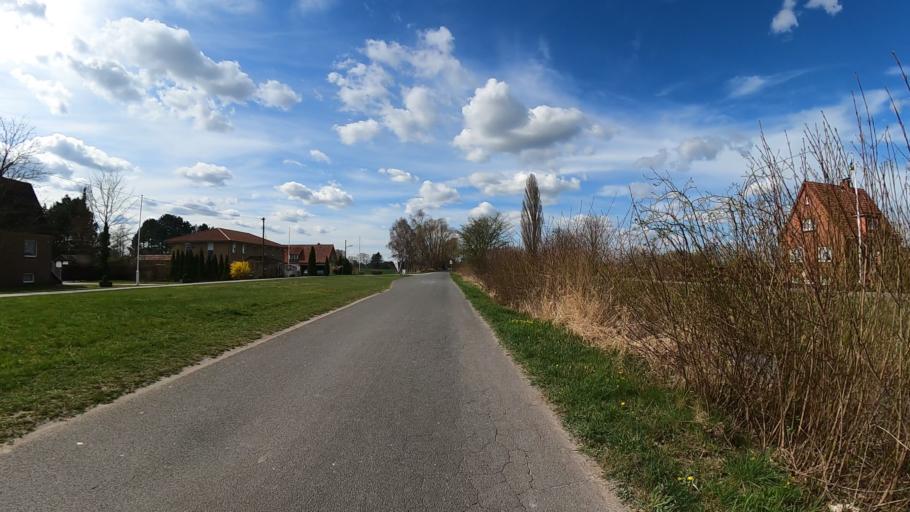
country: DE
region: Lower Saxony
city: Winsen
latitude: 53.4075
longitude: 10.2018
